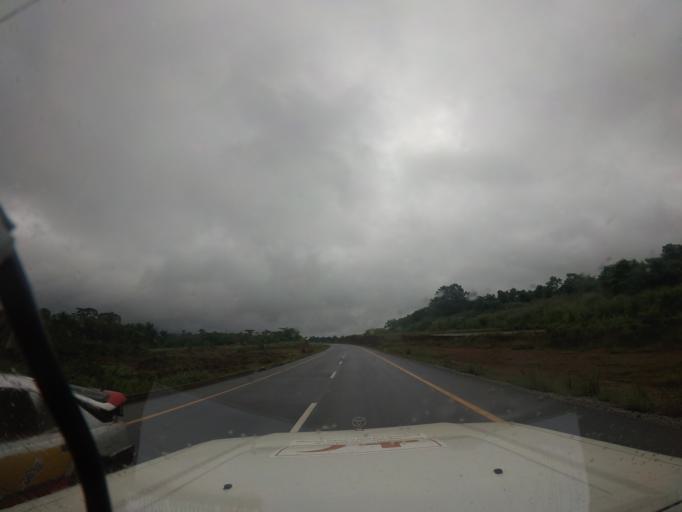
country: SL
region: Eastern Province
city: Hangha
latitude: 7.9304
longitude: -11.1481
